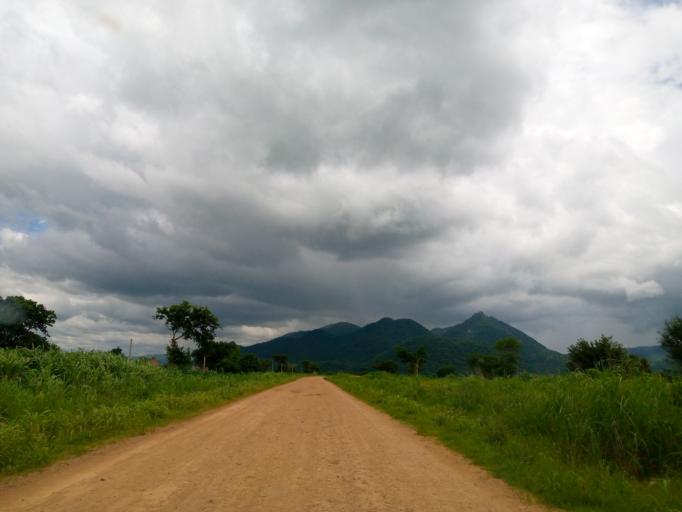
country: ET
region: Oromiya
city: Mendi
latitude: 10.1865
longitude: 35.0931
